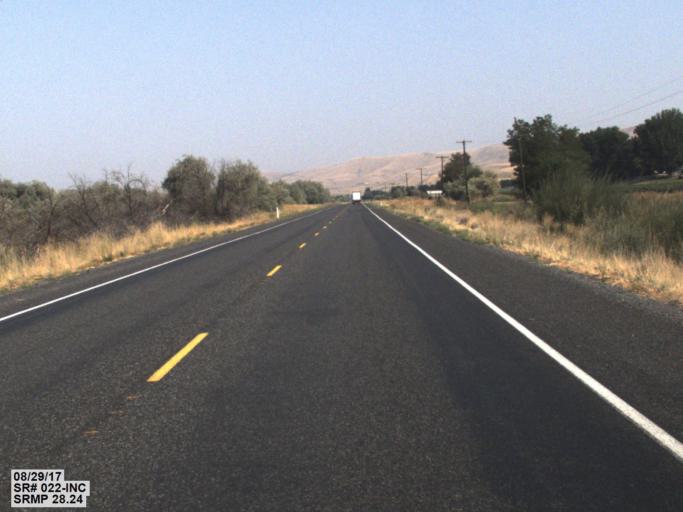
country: US
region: Washington
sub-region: Yakima County
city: Grandview
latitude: 46.1898
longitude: -119.8979
